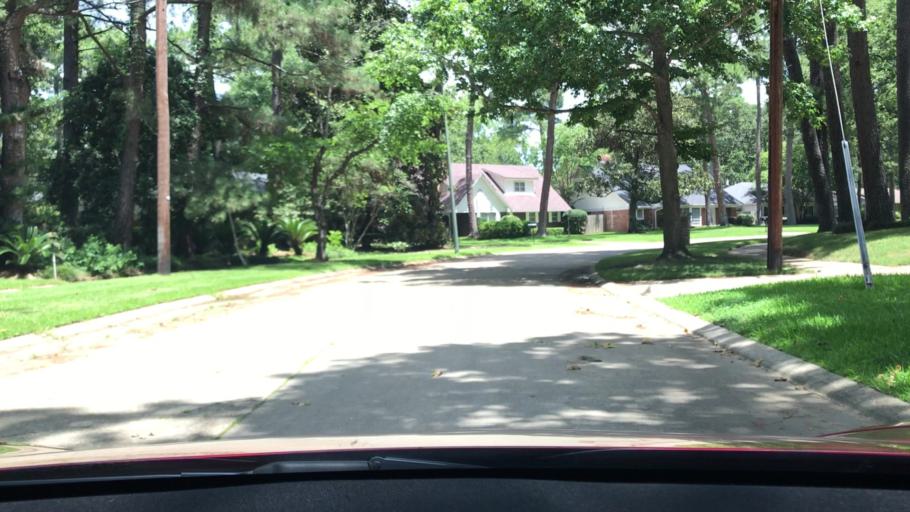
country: US
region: Louisiana
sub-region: Bossier Parish
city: Bossier City
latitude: 32.4284
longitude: -93.7392
